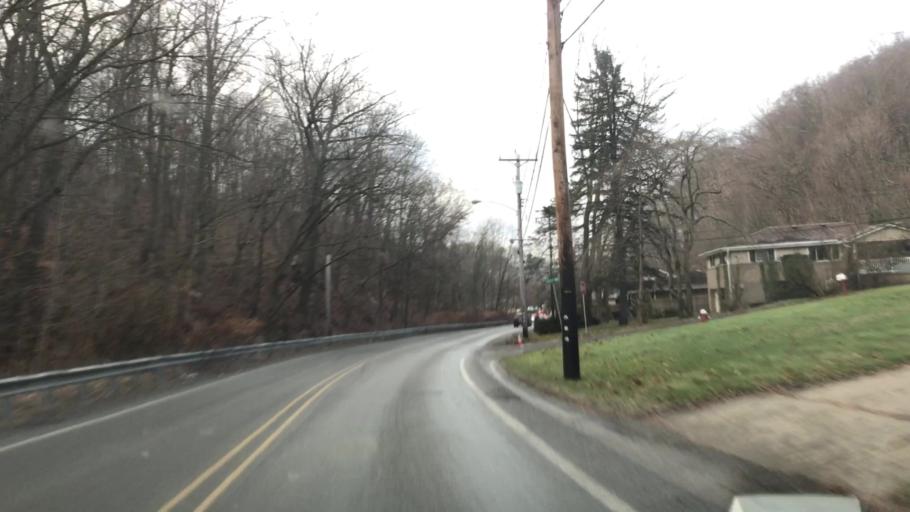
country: US
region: Pennsylvania
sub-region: Allegheny County
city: Avalon
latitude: 40.5099
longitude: -80.0571
